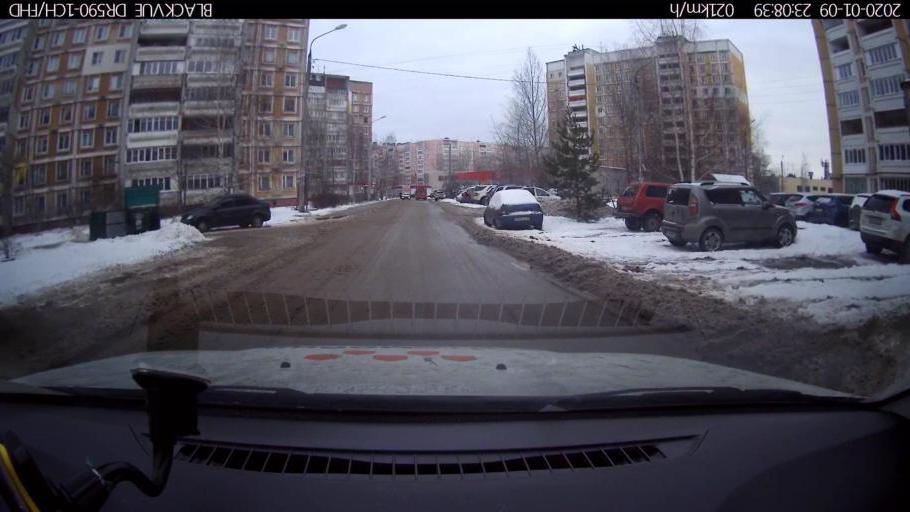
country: RU
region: Nizjnij Novgorod
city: Gorbatovka
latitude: 56.3681
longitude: 43.8003
